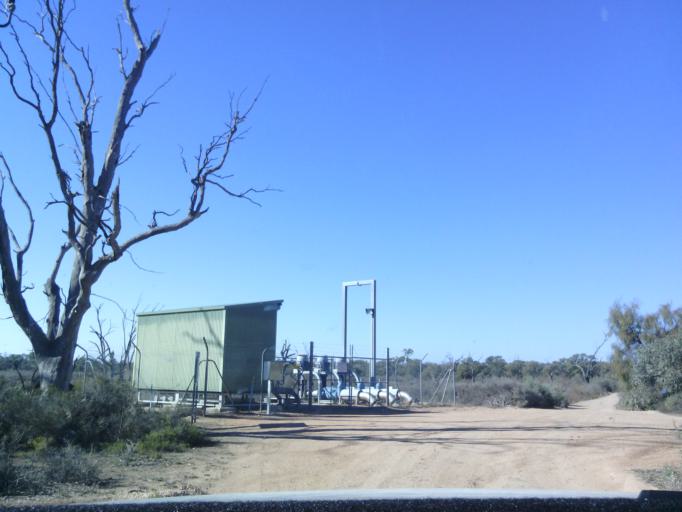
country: AU
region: South Australia
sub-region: Renmark Paringa
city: Renmark West
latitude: -34.2609
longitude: 140.6991
